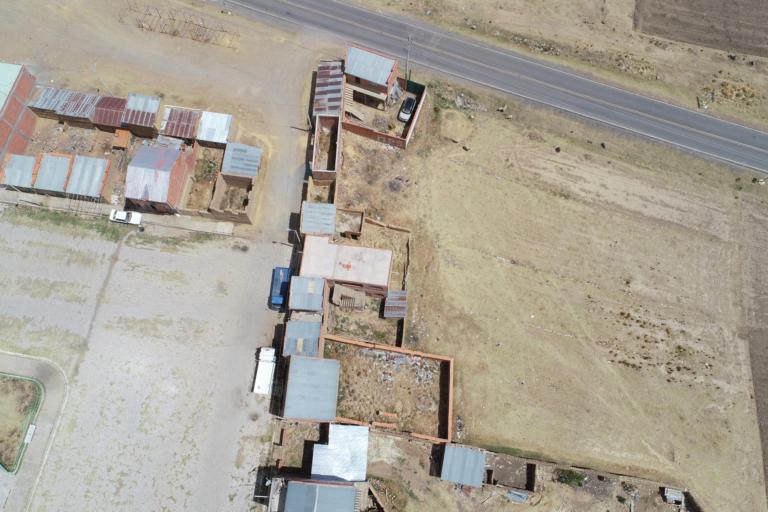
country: BO
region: La Paz
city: Achacachi
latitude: -15.9123
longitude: -68.8849
